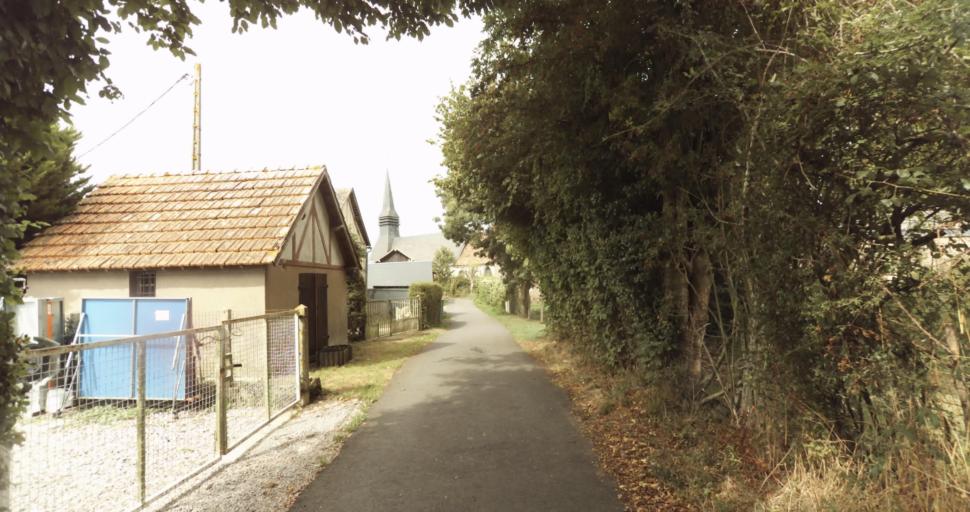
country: FR
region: Lower Normandy
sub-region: Departement du Calvados
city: Orbec
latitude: 48.9405
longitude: 0.3799
